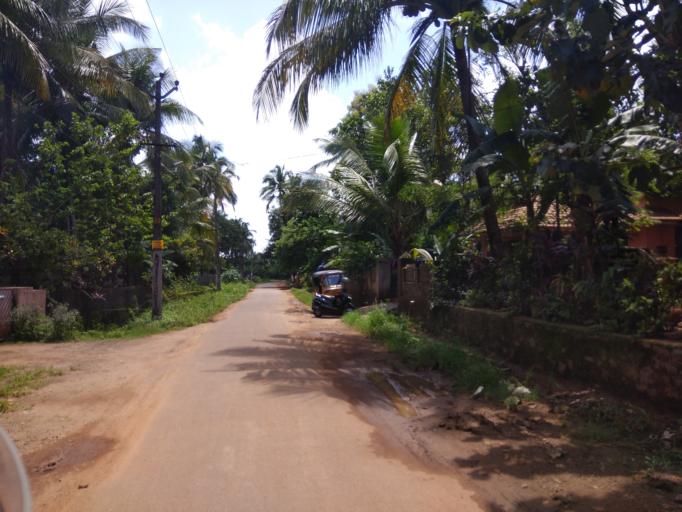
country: IN
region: Kerala
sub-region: Thrissur District
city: Trichur
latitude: 10.5423
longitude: 76.1691
